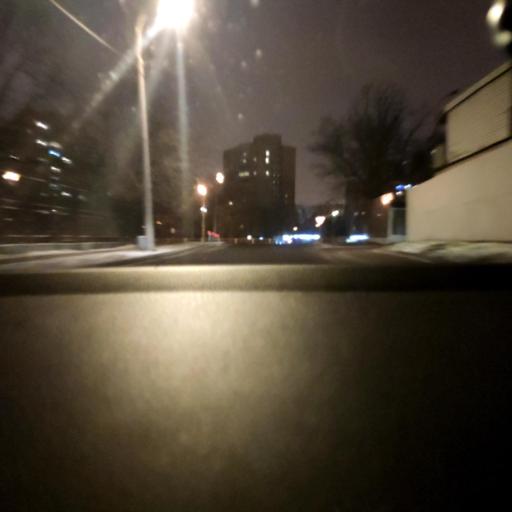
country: RU
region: Moskovskaya
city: Bol'shaya Setun'
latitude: 55.7379
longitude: 37.4388
